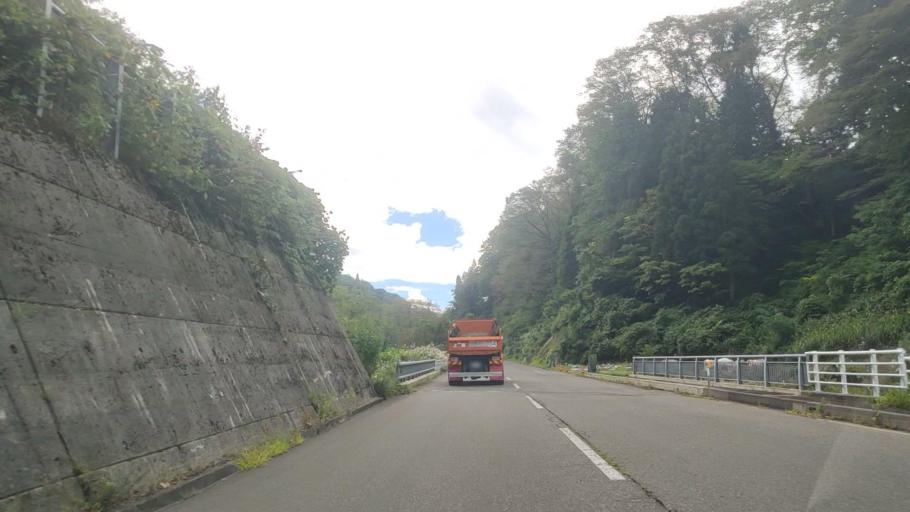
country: JP
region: Nagano
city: Iiyama
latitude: 36.8992
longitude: 138.3189
